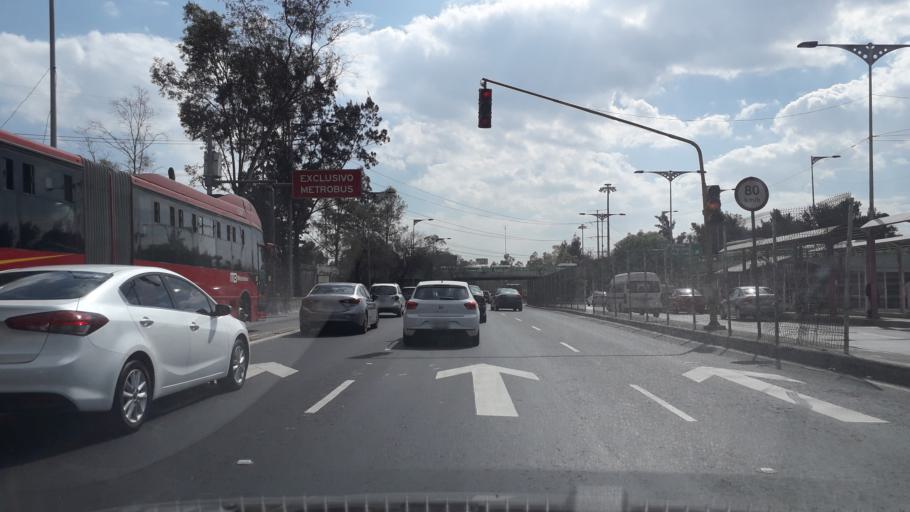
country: MX
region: Mexico
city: Colonia Lindavista
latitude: 19.4949
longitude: -99.1198
